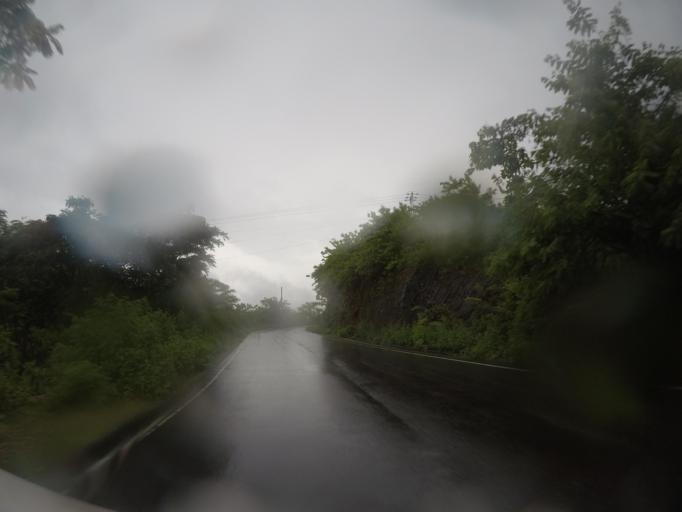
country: TL
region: Bobonaro
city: Maliana
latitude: -8.9567
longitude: 125.0639
